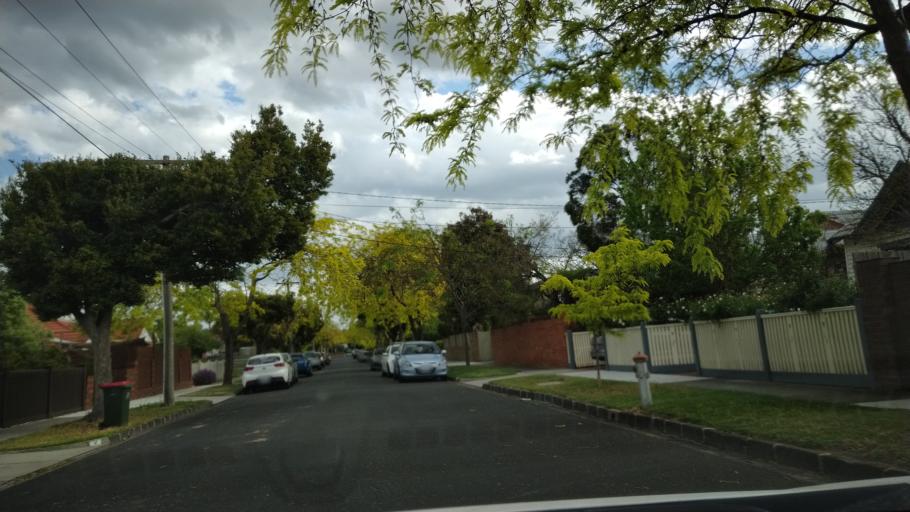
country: AU
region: Victoria
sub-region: Glen Eira
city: Glen Huntly
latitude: -37.8991
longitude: 145.0498
